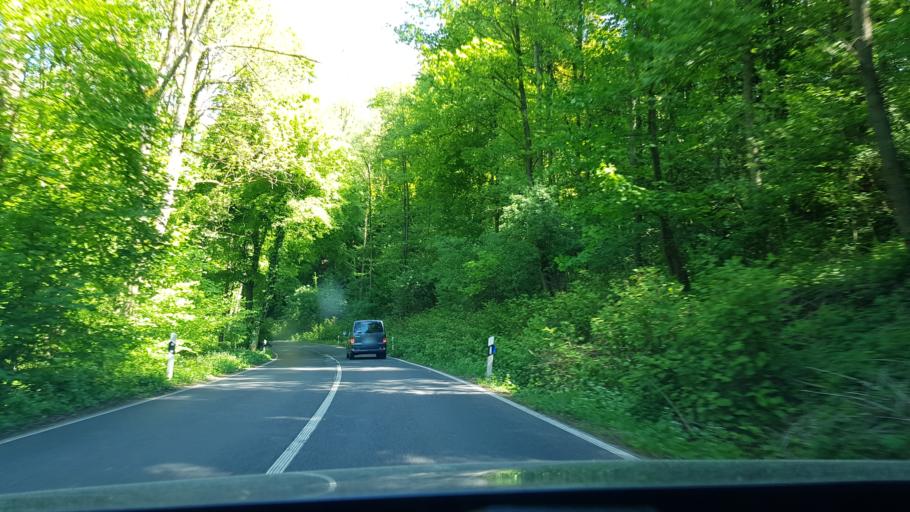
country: DE
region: North Rhine-Westphalia
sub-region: Regierungsbezirk Dusseldorf
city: Heiligenhaus
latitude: 51.3338
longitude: 6.9461
